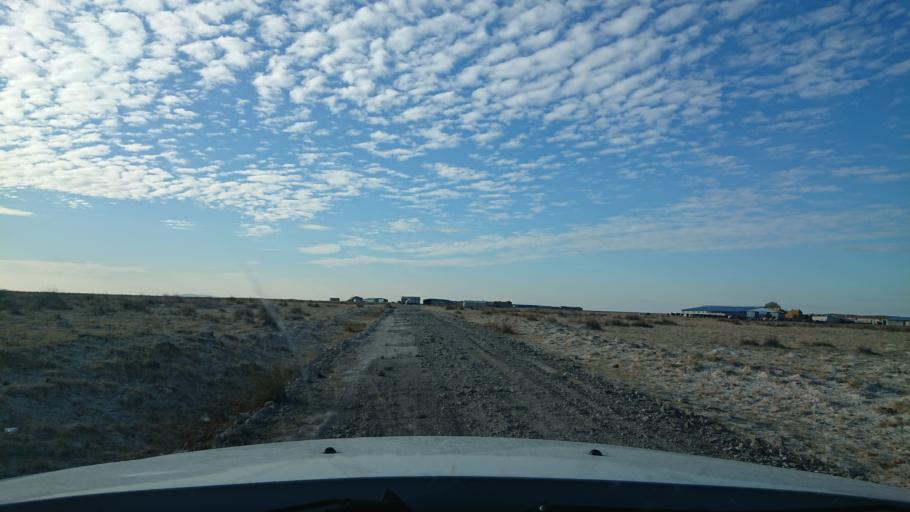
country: TR
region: Aksaray
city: Eskil
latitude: 38.5665
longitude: 33.2978
